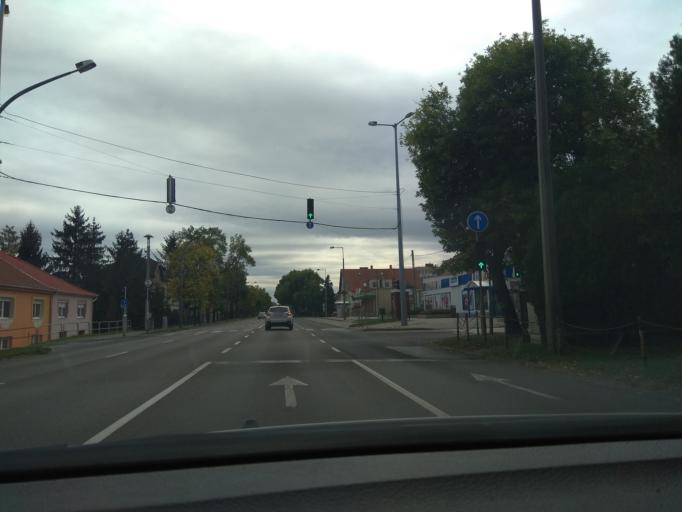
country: HU
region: Heves
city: Eger
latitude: 47.8799
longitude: 20.3818
